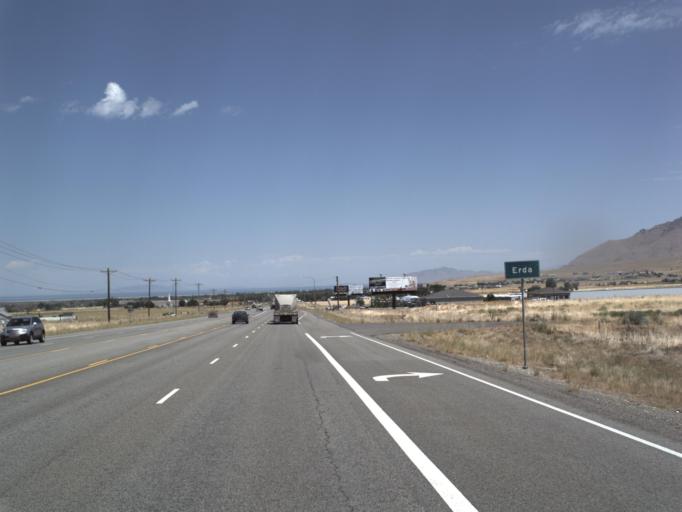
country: US
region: Utah
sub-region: Tooele County
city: Erda
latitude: 40.5873
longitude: -112.2938
